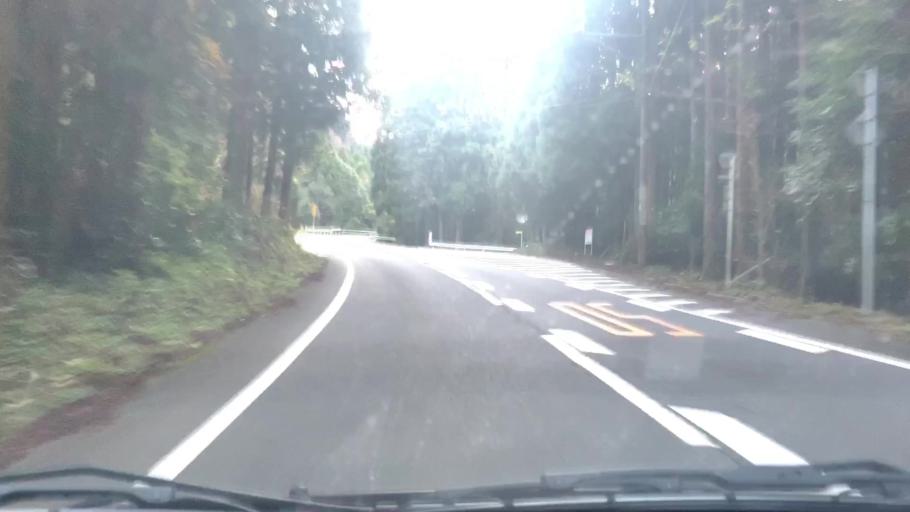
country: JP
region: Saga Prefecture
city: Kashima
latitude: 33.0140
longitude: 130.0650
